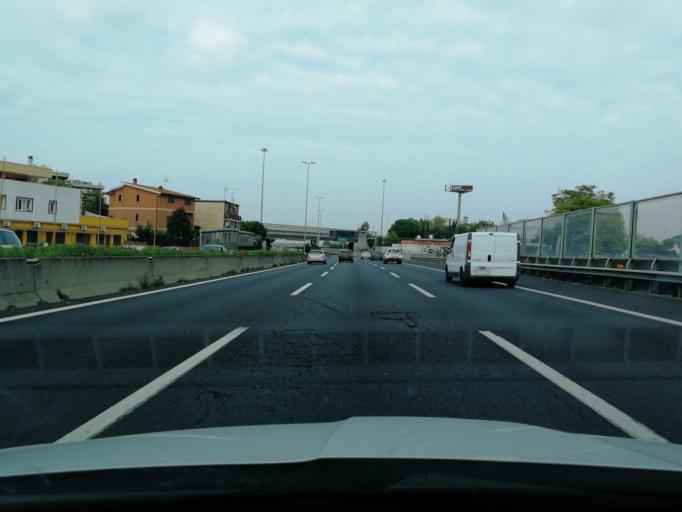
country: IT
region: Latium
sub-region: Citta metropolitana di Roma Capitale
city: Ciampino
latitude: 41.8462
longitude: 12.5951
